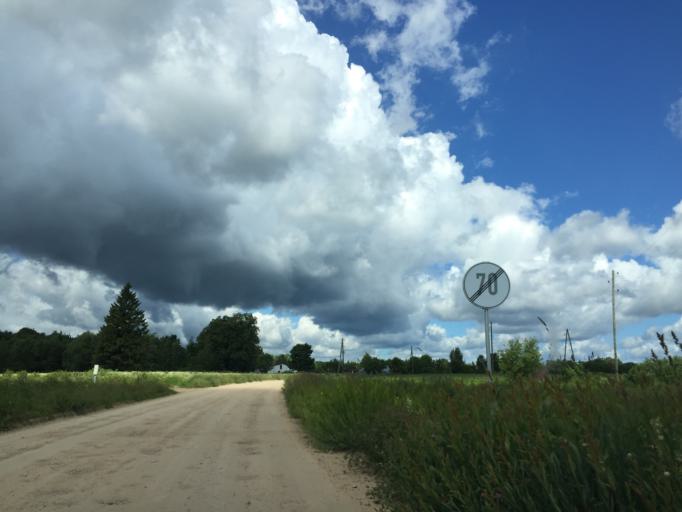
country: LV
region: Lecava
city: Iecava
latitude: 56.6228
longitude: 24.1873
